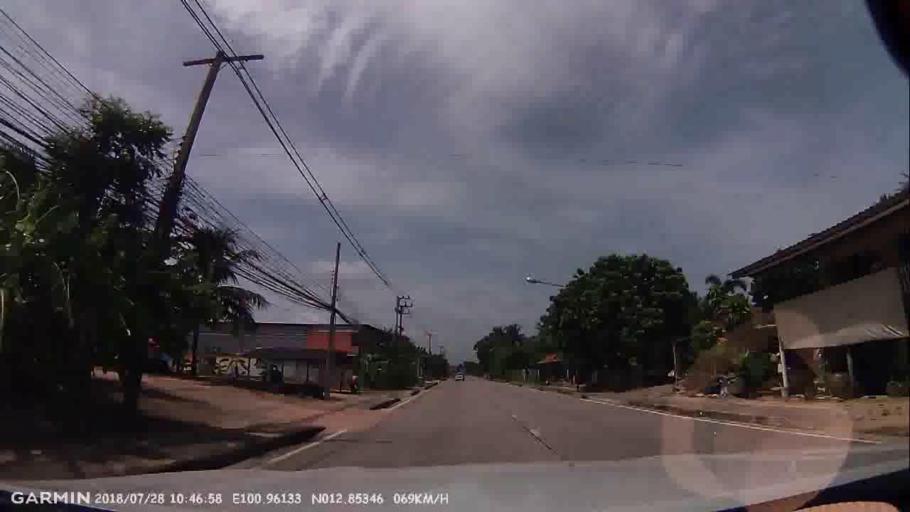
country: TH
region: Chon Buri
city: Phatthaya
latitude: 12.8533
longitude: 100.9613
